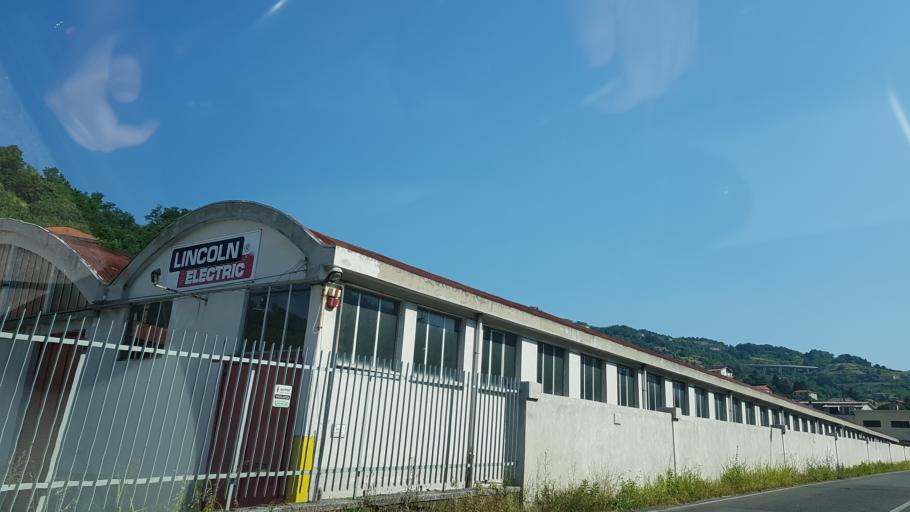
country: IT
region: Liguria
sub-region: Provincia di Genova
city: Pedemonte
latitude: 44.5021
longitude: 8.9264
